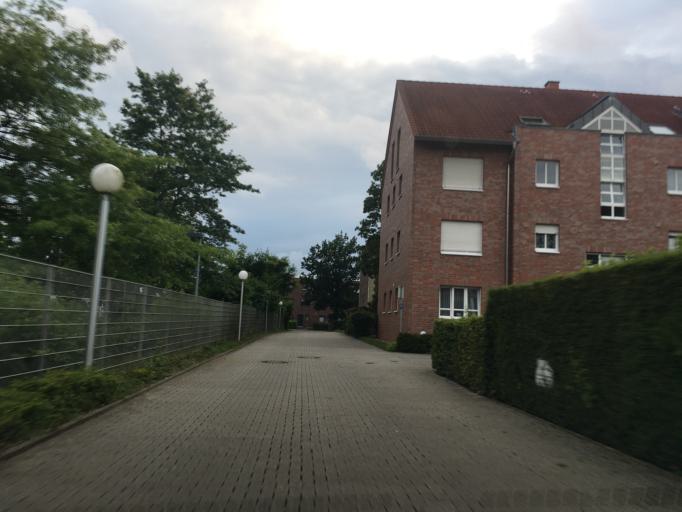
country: DE
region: North Rhine-Westphalia
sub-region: Regierungsbezirk Munster
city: Muenster
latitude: 51.9503
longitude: 7.6675
